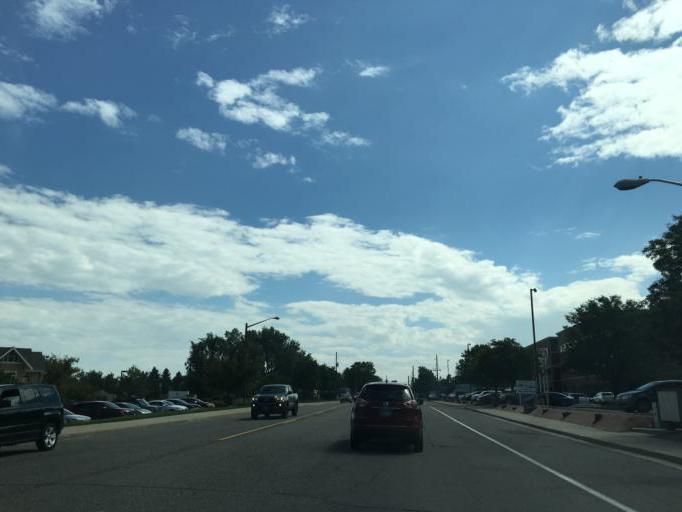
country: US
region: Colorado
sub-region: Jefferson County
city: Applewood
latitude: 39.7578
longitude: -105.1426
